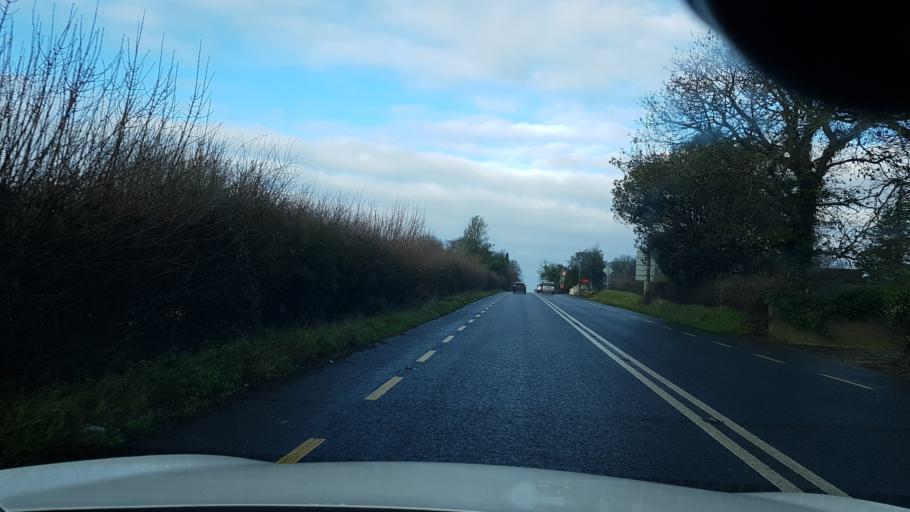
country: IE
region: Leinster
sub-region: An Mhi
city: Navan
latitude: 53.6052
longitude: -6.6223
